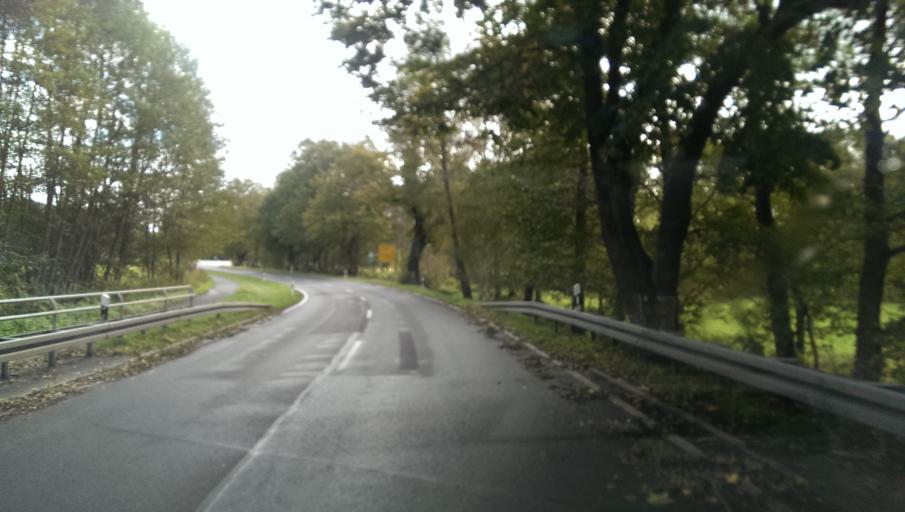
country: DE
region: Brandenburg
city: Luckenwalde
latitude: 52.0625
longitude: 13.1563
